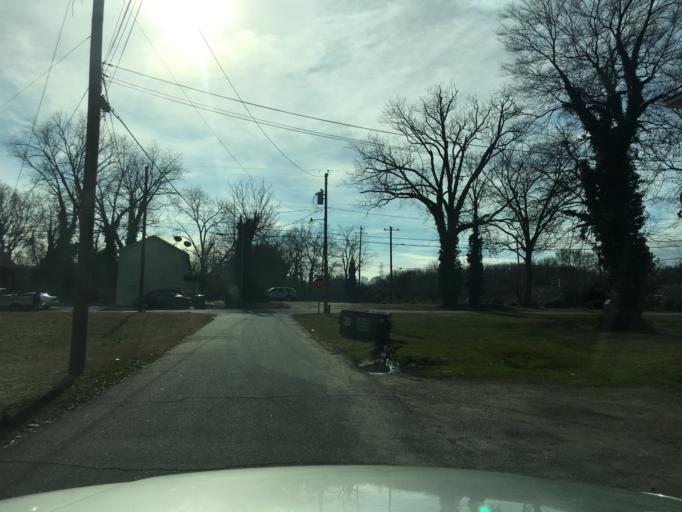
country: US
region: South Carolina
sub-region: Greenville County
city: Greenville
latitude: 34.8571
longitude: -82.4128
